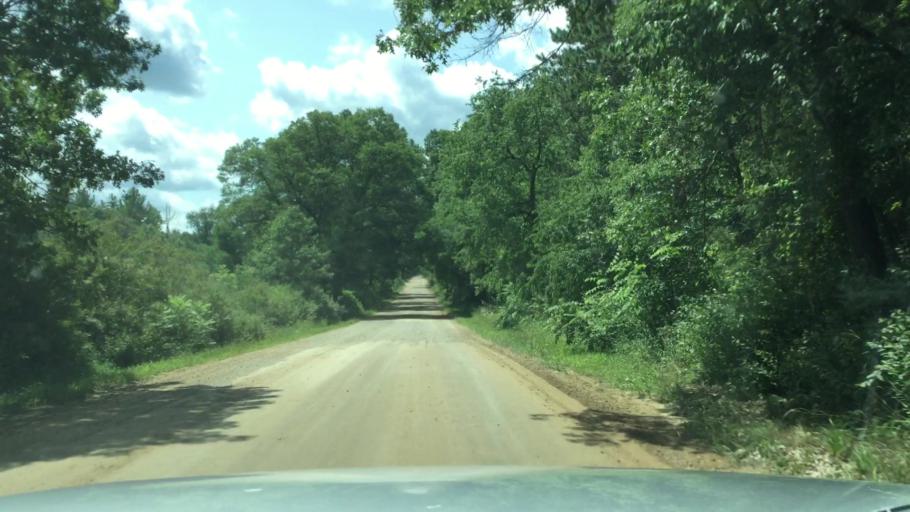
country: US
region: Michigan
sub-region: Ionia County
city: Belding
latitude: 43.1331
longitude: -85.2134
